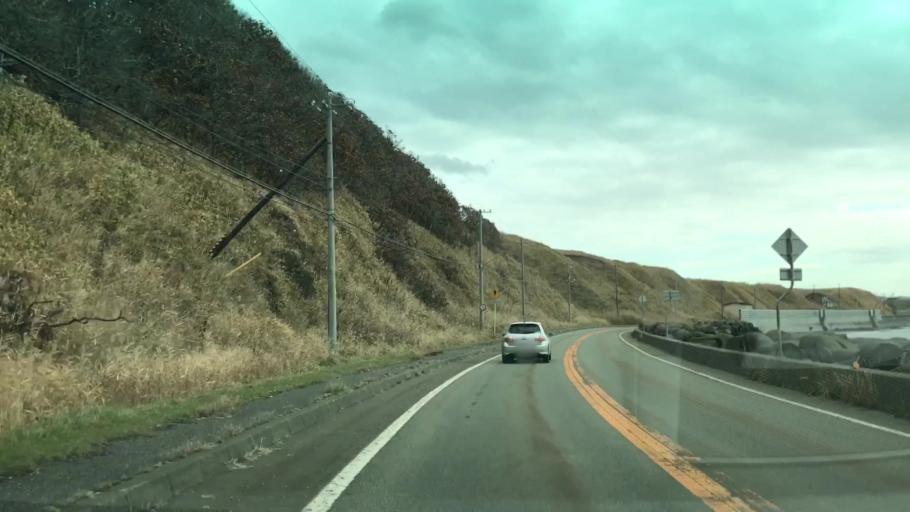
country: JP
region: Hokkaido
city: Shizunai-furukawacho
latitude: 42.0509
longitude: 143.0936
